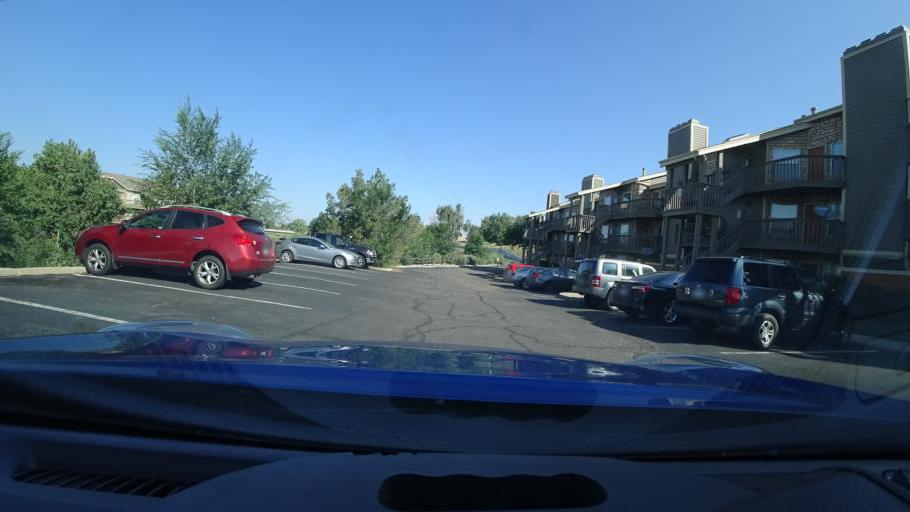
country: US
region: Colorado
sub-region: Adams County
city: Aurora
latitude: 39.7185
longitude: -104.8066
